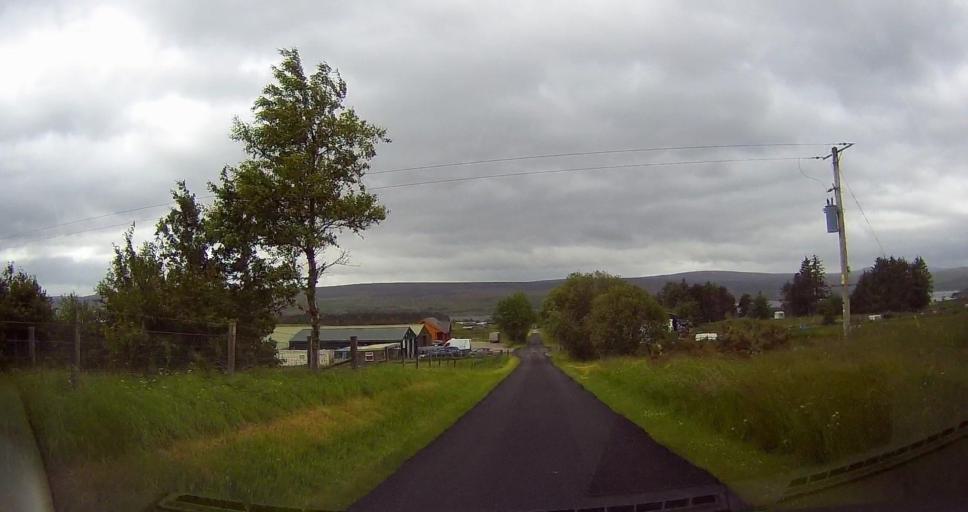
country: GB
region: Scotland
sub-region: Highland
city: Evanton
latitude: 58.0802
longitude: -4.4544
